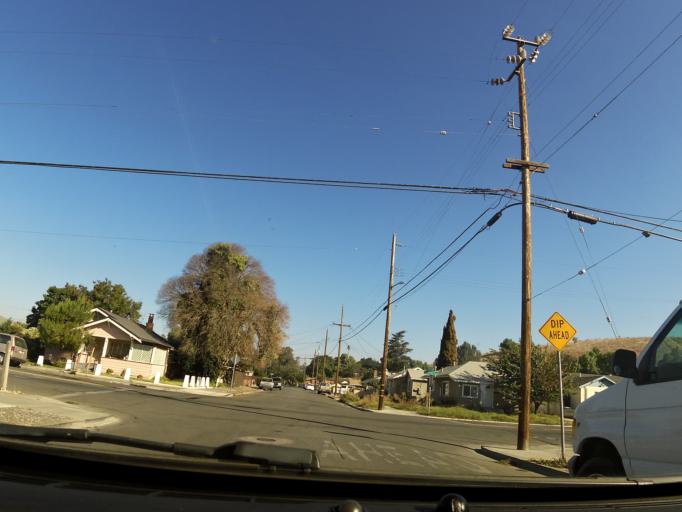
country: US
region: California
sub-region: San Benito County
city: Hollister
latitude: 36.8539
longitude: -121.4094
